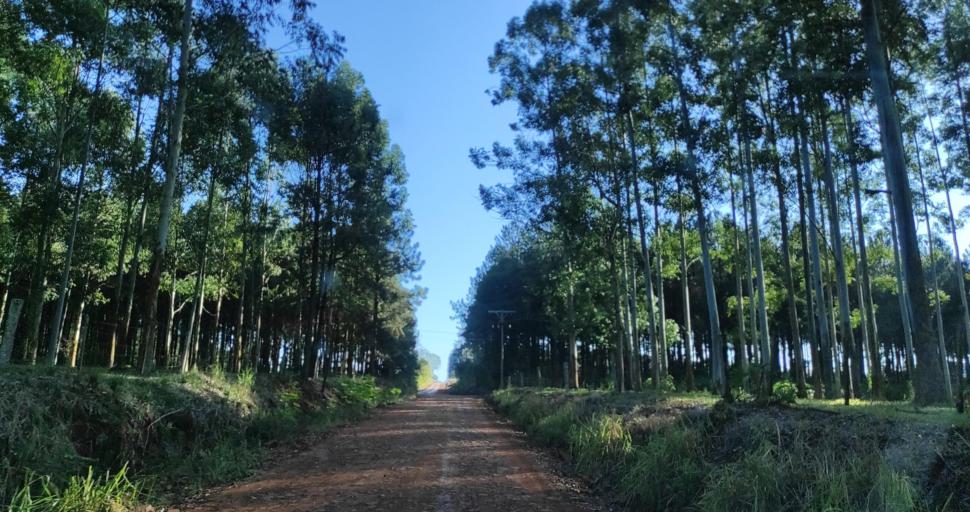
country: AR
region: Misiones
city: Puerto Rico
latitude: -26.8626
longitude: -55.0149
